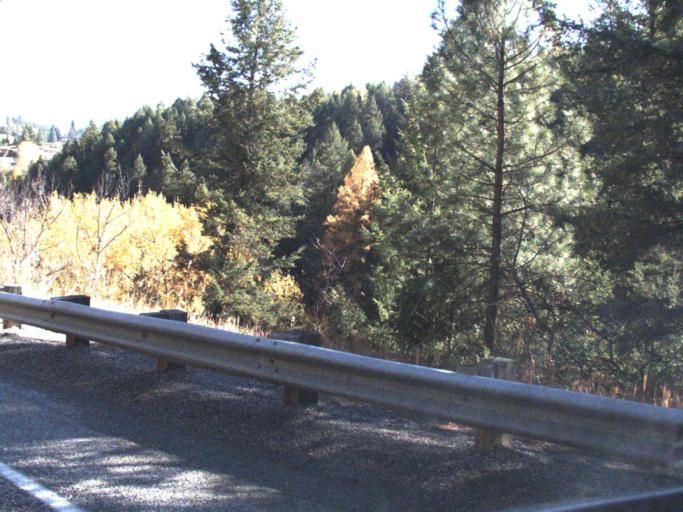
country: US
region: Washington
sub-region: Ferry County
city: Republic
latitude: 48.6489
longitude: -118.7488
